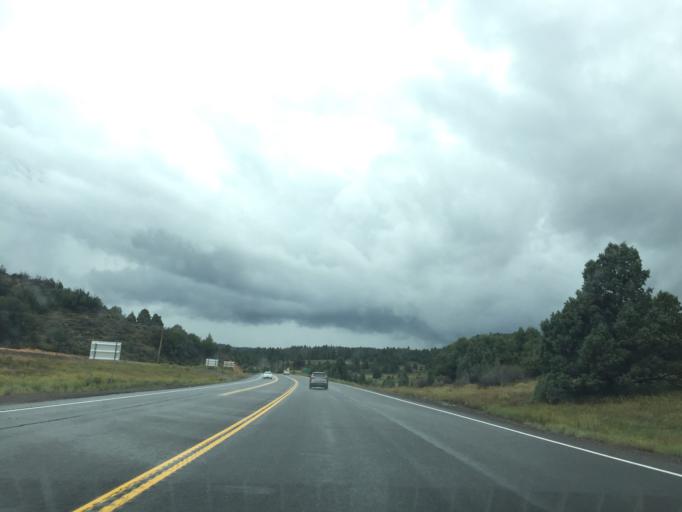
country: US
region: Utah
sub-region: Garfield County
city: Panguitch
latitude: 37.4880
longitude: -112.5130
